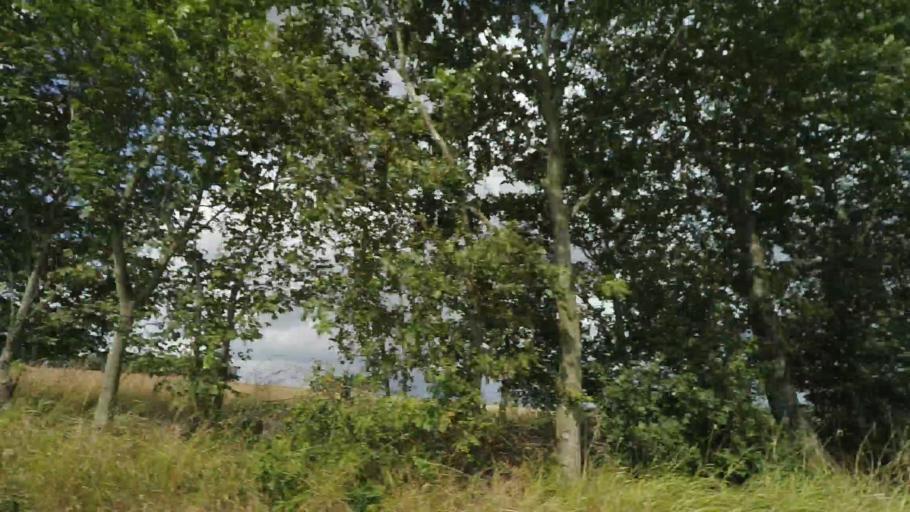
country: DK
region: Central Jutland
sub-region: Norddjurs Kommune
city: Allingabro
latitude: 56.5325
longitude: 10.3586
